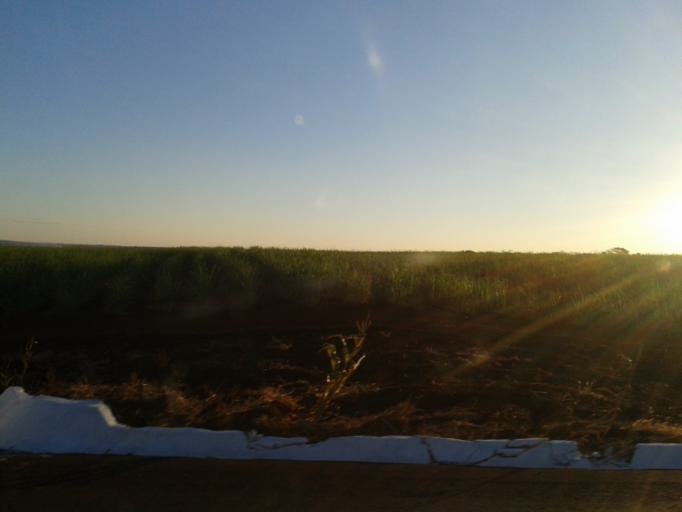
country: BR
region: Minas Gerais
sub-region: Centralina
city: Centralina
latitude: -18.7128
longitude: -49.2789
